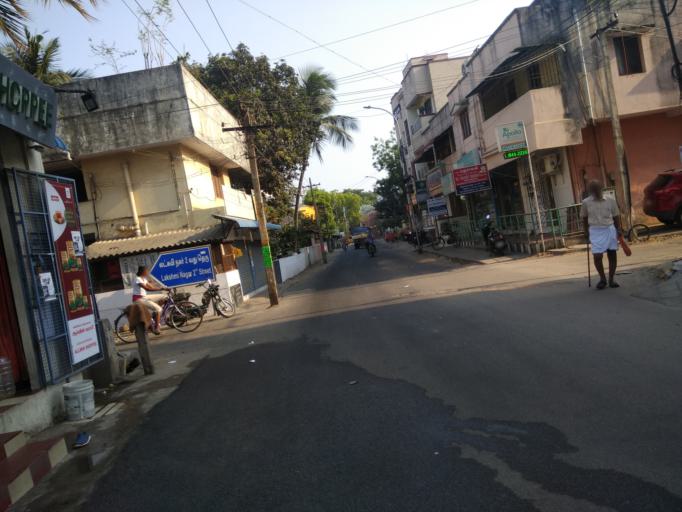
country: IN
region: Tamil Nadu
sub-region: Kancheepuram
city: Madipakkam
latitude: 12.9797
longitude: 80.1881
